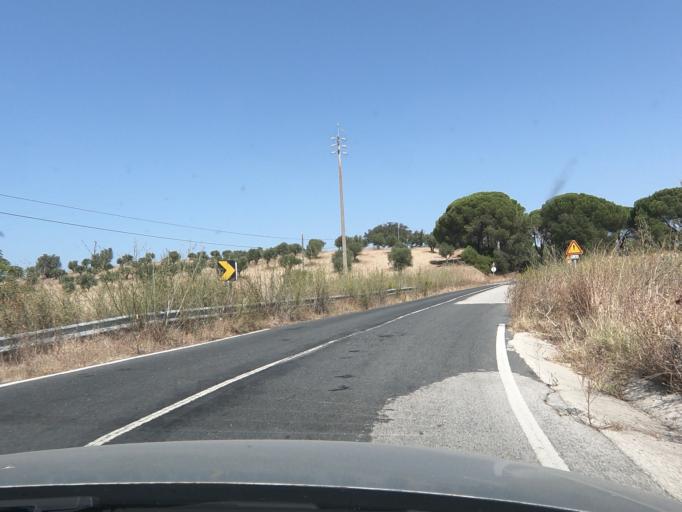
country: PT
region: Setubal
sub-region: Alcacer do Sal
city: Alcacer do Sal
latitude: 38.2878
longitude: -8.4048
